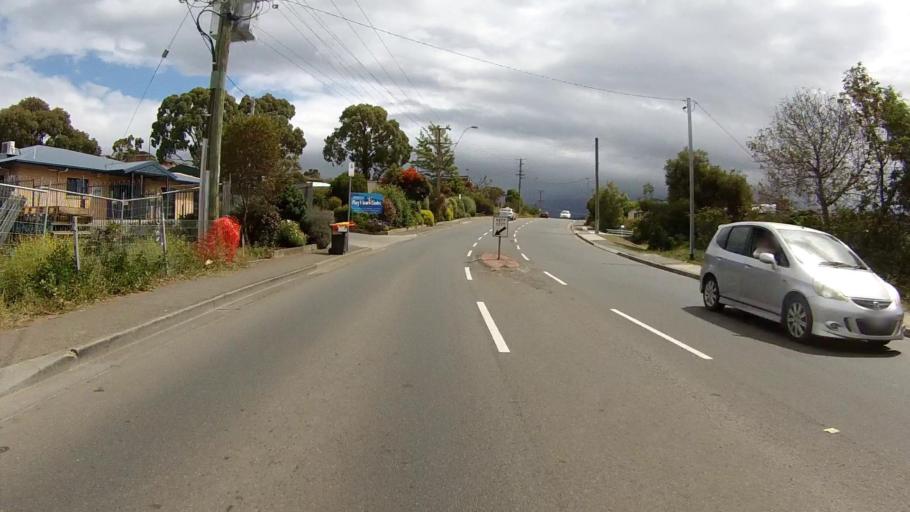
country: AU
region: Tasmania
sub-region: Clarence
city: Warrane
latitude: -42.8634
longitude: 147.3775
